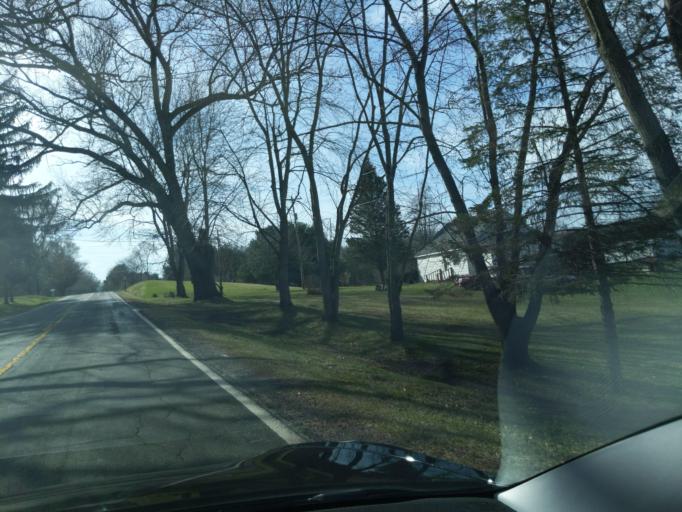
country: US
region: Michigan
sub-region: Ingham County
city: Stockbridge
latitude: 42.4899
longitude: -84.3001
